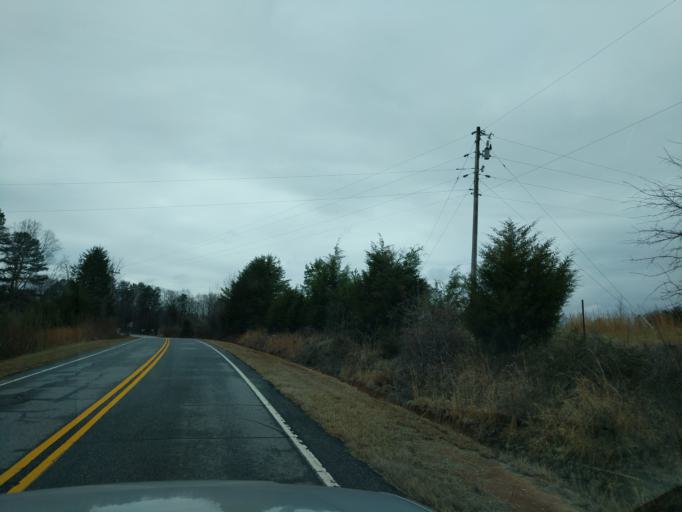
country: US
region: South Carolina
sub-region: Oconee County
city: Walhalla
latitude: 34.7919
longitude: -83.0804
